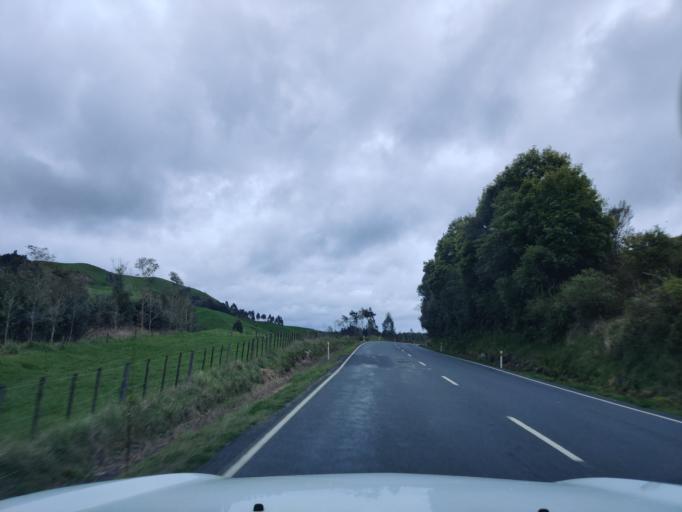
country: NZ
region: Waikato
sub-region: Otorohanga District
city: Otorohanga
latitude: -38.5362
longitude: 175.1781
